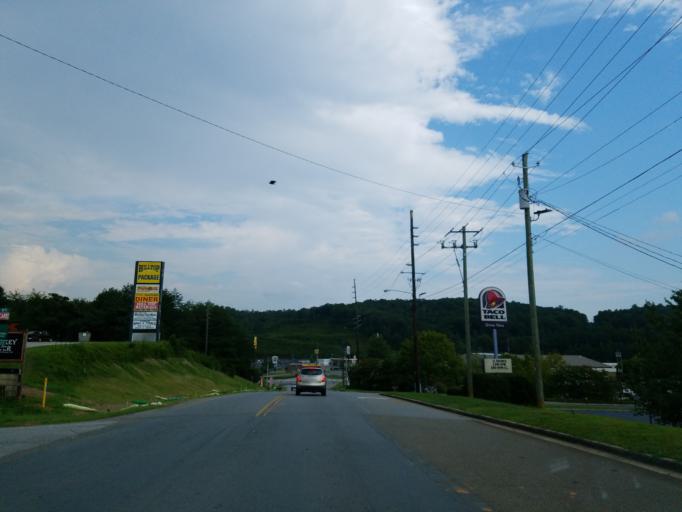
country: US
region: Georgia
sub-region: Gilmer County
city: Ellijay
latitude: 34.6787
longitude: -84.4814
